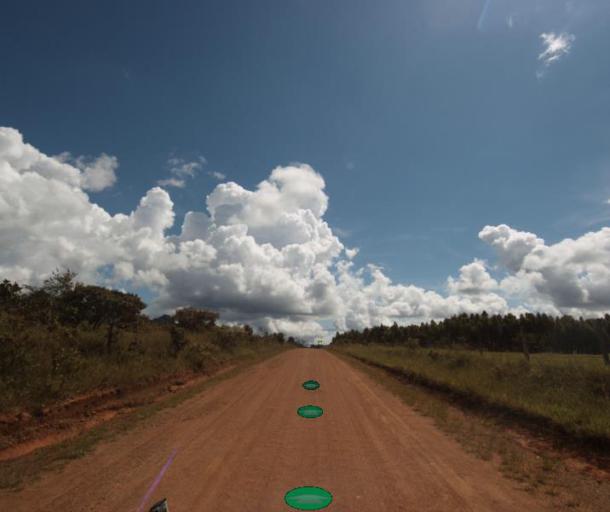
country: BR
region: Goias
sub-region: Pirenopolis
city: Pirenopolis
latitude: -15.7811
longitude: -48.8188
